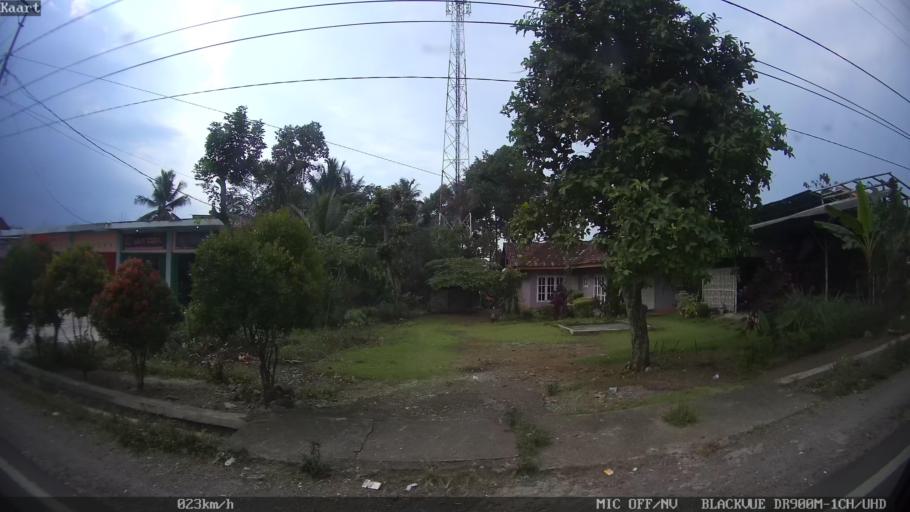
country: ID
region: Lampung
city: Natar
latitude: -5.3660
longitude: 105.1622
